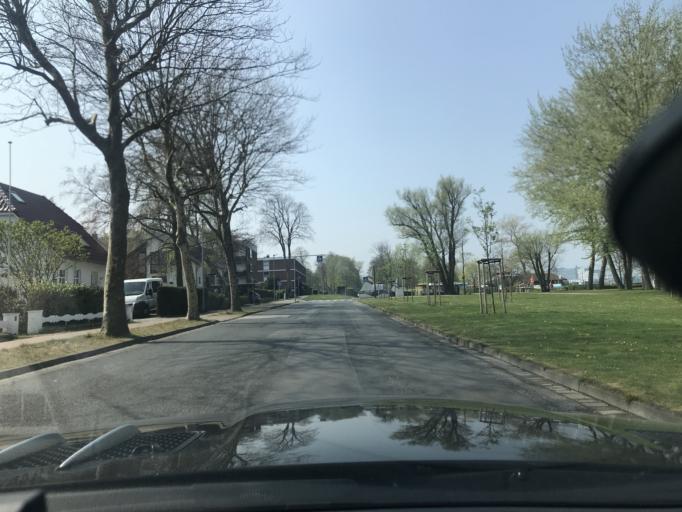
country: DE
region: Schleswig-Holstein
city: Heiligenhafen
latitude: 54.3743
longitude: 10.9732
